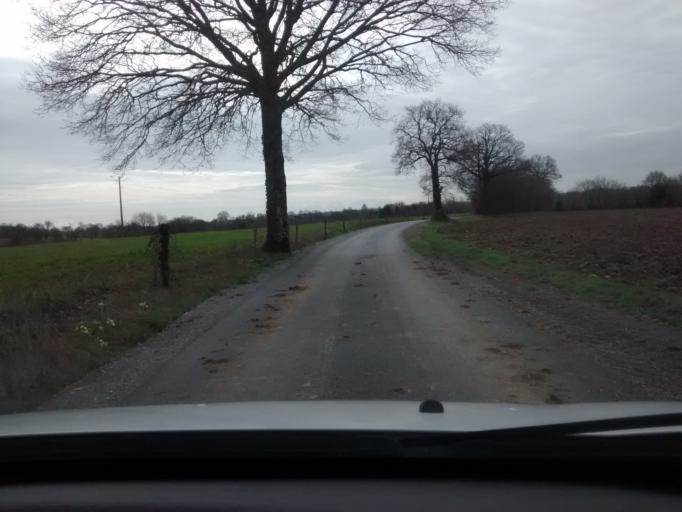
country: FR
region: Brittany
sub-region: Departement d'Ille-et-Vilaine
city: Liffre
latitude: 48.2106
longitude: -1.4768
